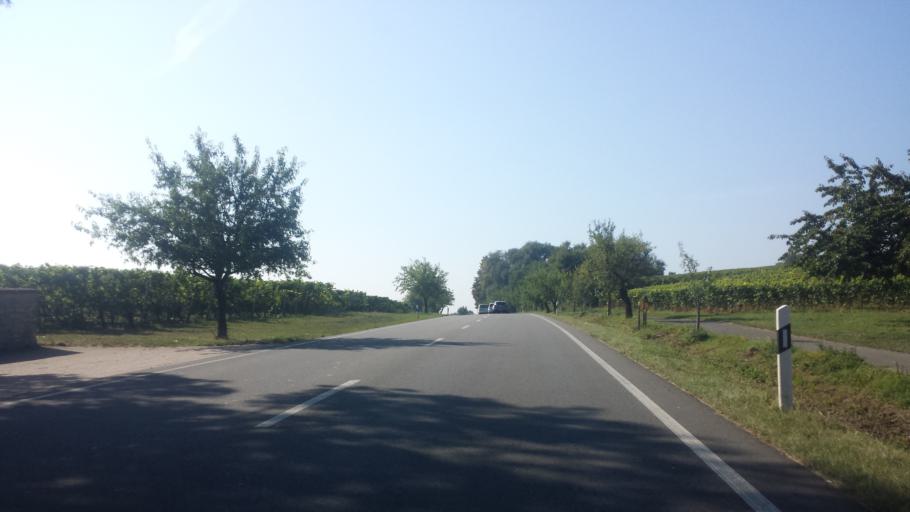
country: DE
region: Rheinland-Pfalz
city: Bockenheim
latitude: 49.5982
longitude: 8.1794
